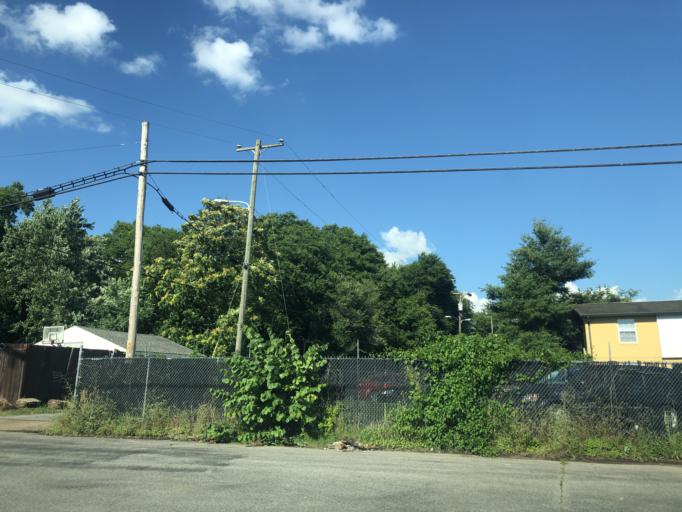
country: US
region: Tennessee
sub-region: Davidson County
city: Nashville
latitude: 36.1797
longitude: -86.7720
